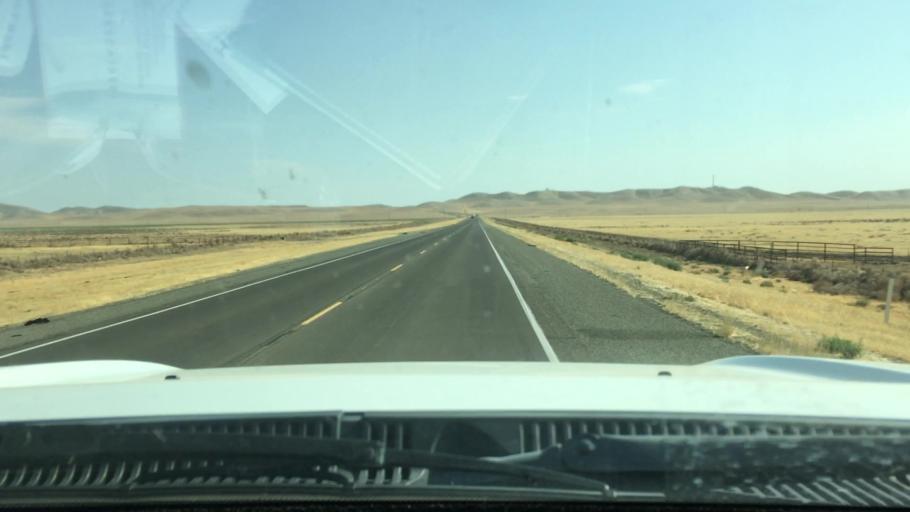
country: US
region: California
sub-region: Kings County
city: Avenal
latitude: 35.8229
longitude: -120.0940
